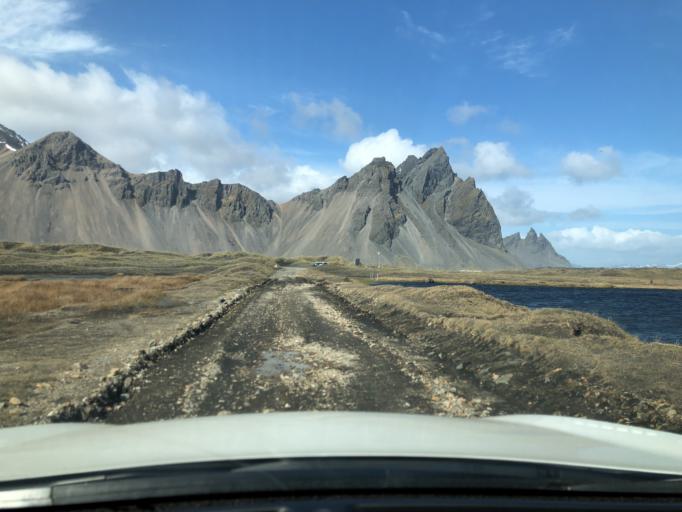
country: IS
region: East
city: Hoefn
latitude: 64.2429
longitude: -14.9716
